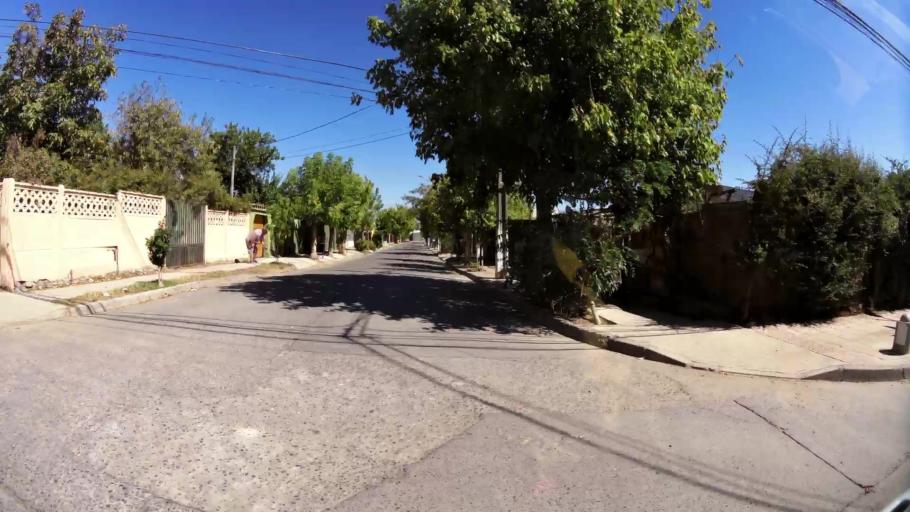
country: CL
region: O'Higgins
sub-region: Provincia de Cachapoal
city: Rancagua
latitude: -34.1686
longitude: -70.7071
